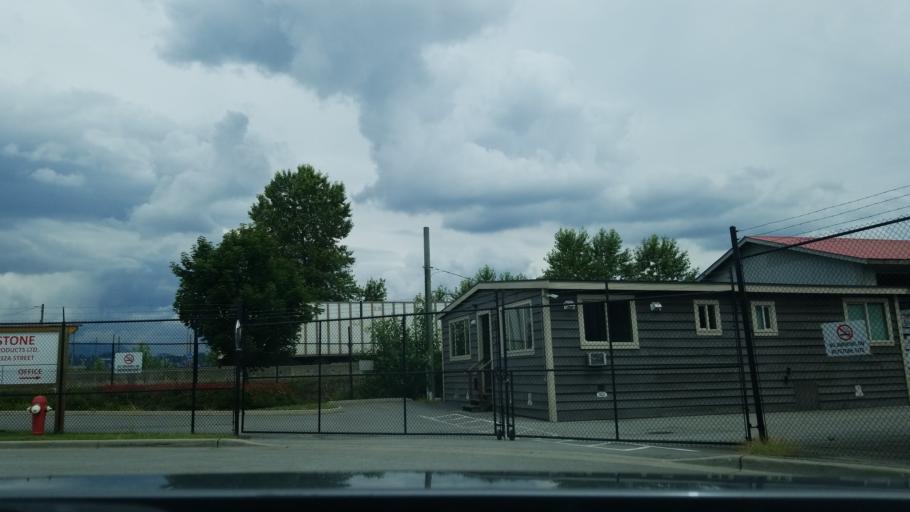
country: CA
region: British Columbia
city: New Westminster
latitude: 49.2129
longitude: -122.8550
